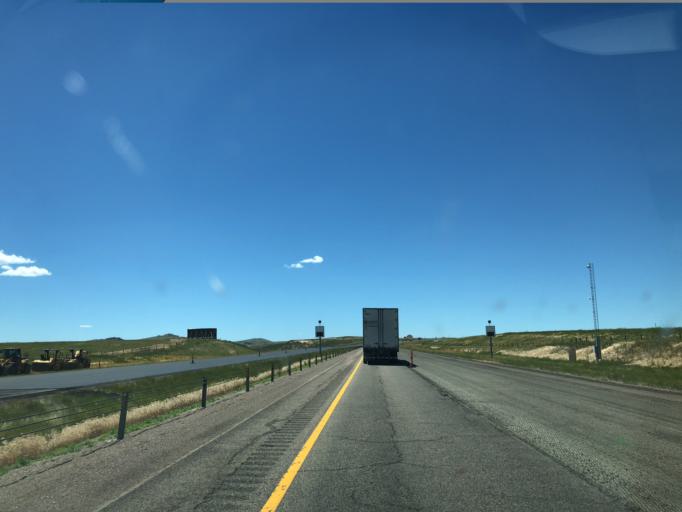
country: US
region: Wyoming
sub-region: Laramie County
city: Cheyenne
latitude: 41.0988
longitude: -105.1304
